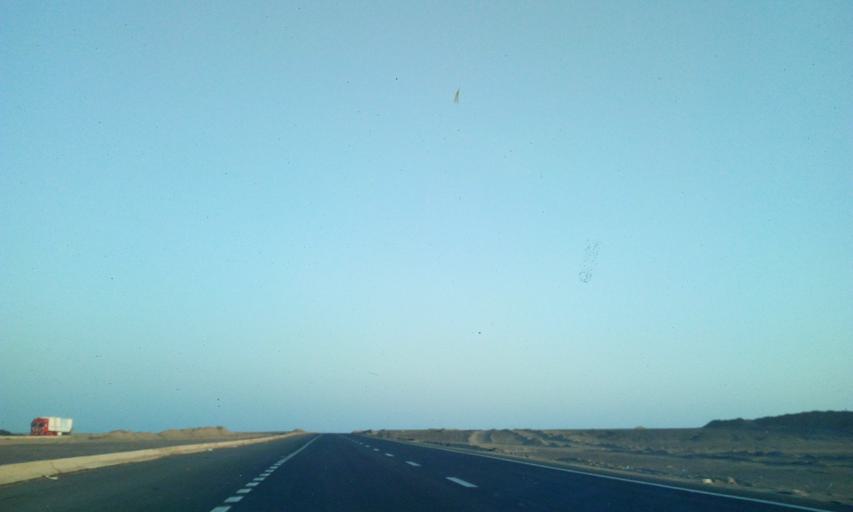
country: EG
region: Red Sea
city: El Gouna
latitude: 27.7849
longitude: 33.4783
